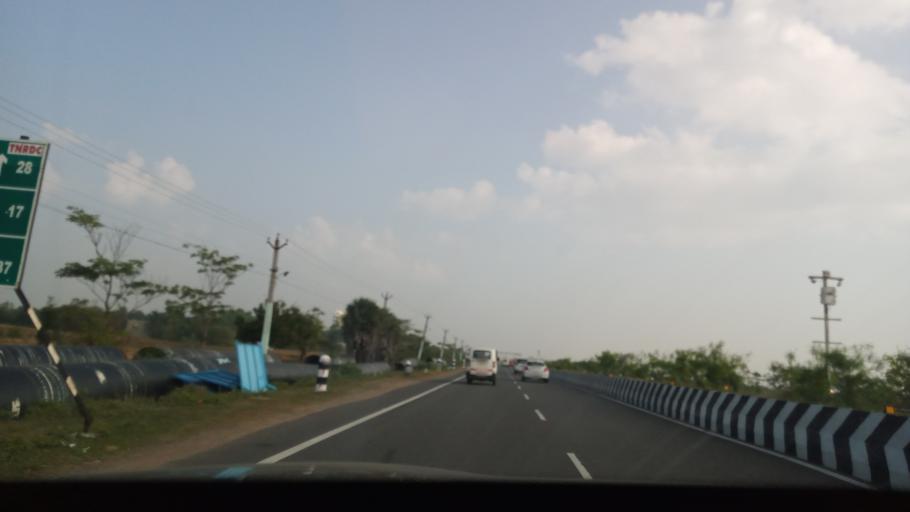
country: IN
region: Tamil Nadu
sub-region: Kancheepuram
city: Injambakkam
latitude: 12.7645
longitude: 80.2459
